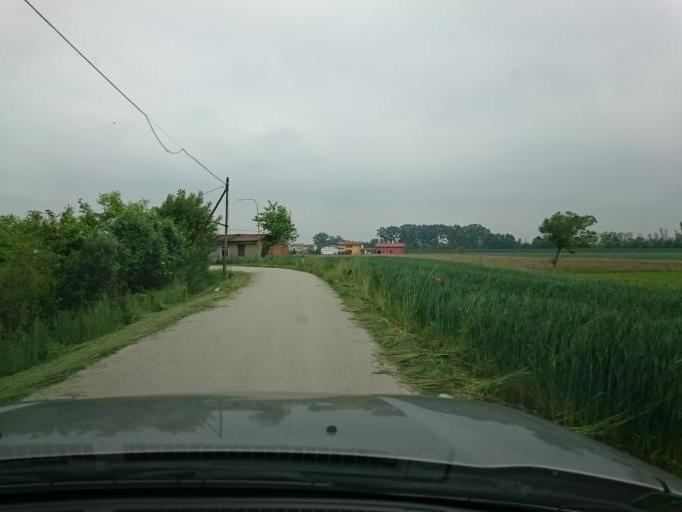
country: IT
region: Veneto
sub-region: Provincia di Padova
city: Cartura
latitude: 45.2932
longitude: 11.8561
